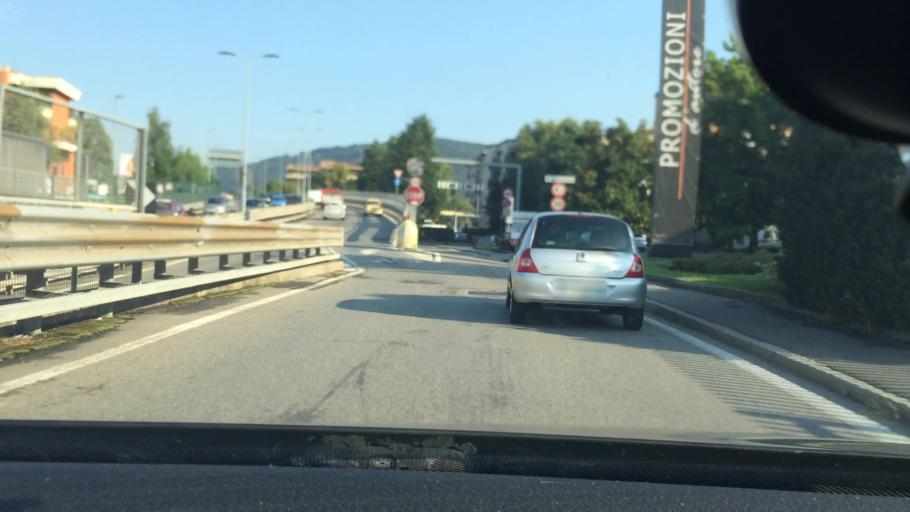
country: IT
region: Lombardy
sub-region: Provincia di Bergamo
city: Torre Boldone
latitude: 45.7064
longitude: 9.6940
